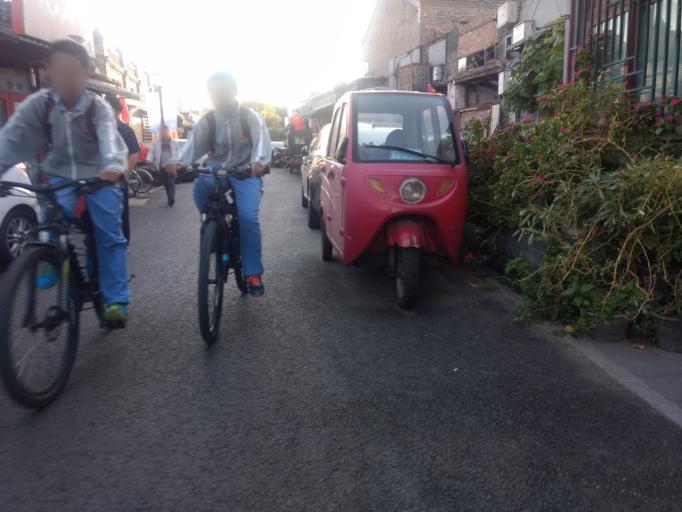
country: CN
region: Beijing
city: Beijing
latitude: 39.8906
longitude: 116.3799
